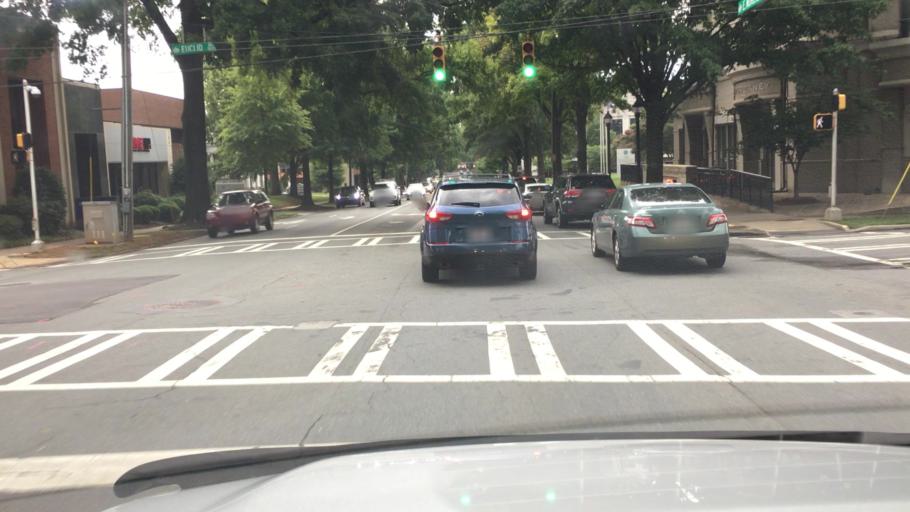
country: US
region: North Carolina
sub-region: Mecklenburg County
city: Charlotte
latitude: 35.2161
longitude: -80.8468
